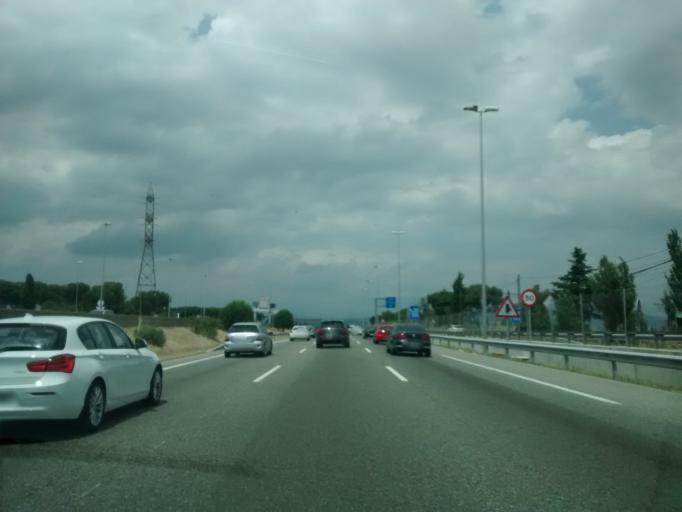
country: ES
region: Madrid
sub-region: Provincia de Madrid
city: Las Rozas de Madrid
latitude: 40.5126
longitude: -3.8811
